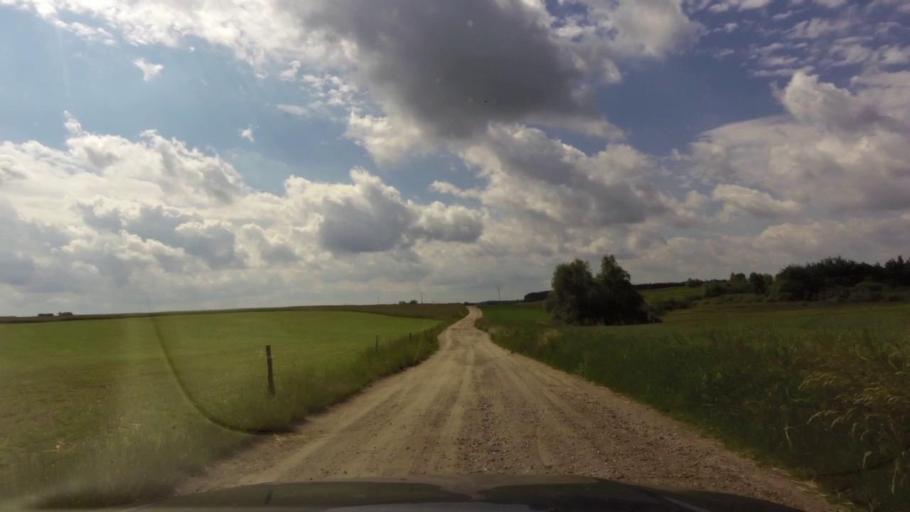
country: PL
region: West Pomeranian Voivodeship
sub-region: Powiat pyrzycki
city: Lipiany
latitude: 52.9650
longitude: 14.9312
